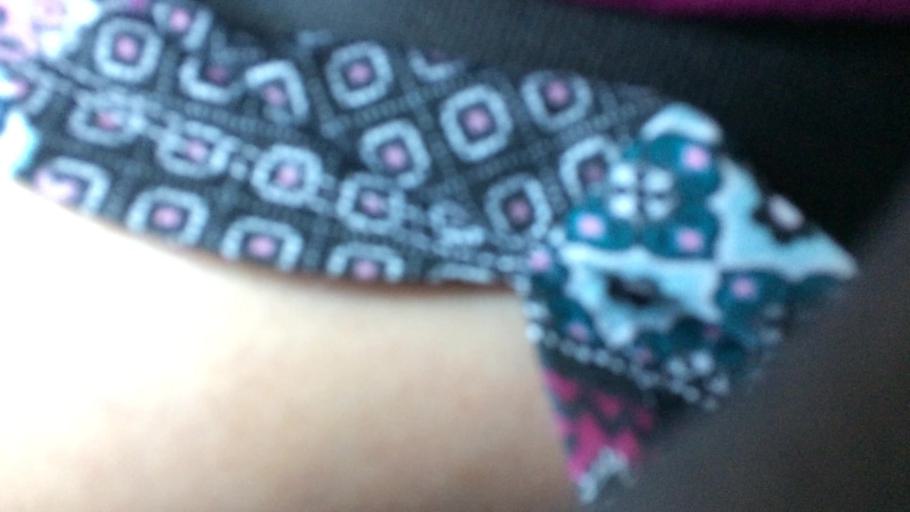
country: US
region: New Mexico
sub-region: Colfax County
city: Springer
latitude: 35.9641
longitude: -104.7597
